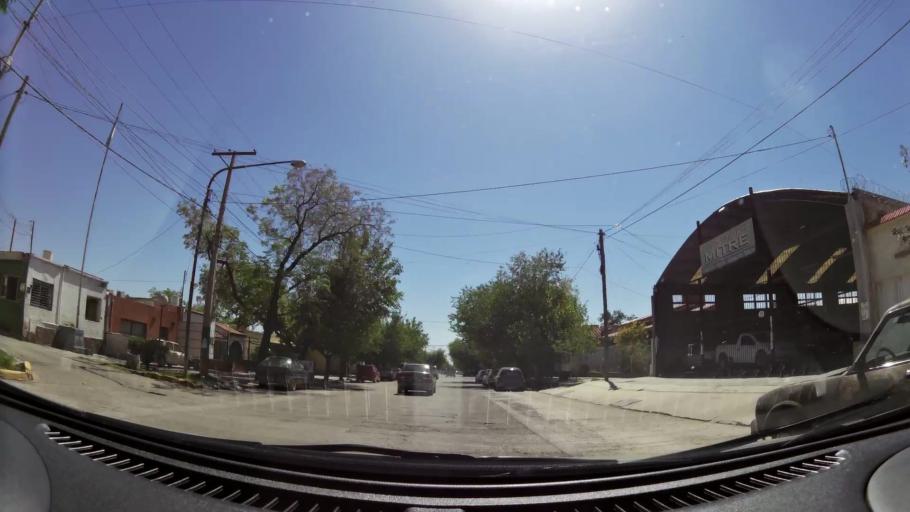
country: AR
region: Mendoza
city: Mendoza
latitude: -32.8931
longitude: -68.8172
